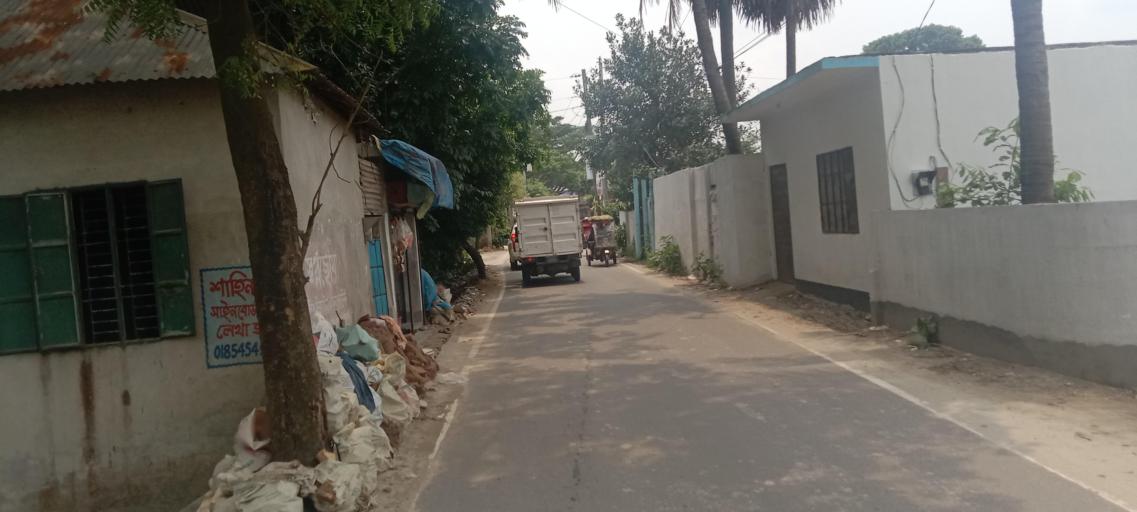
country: BD
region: Dhaka
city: Azimpur
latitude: 23.7184
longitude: 90.3450
